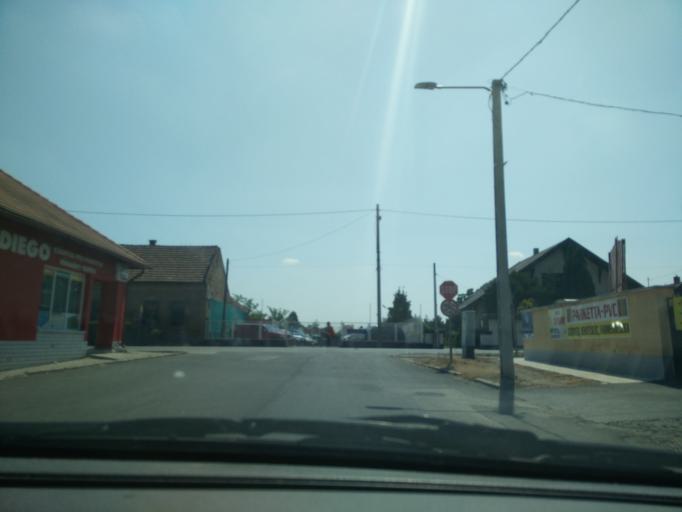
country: HU
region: Heves
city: Hatvan
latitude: 47.6665
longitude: 19.6973
